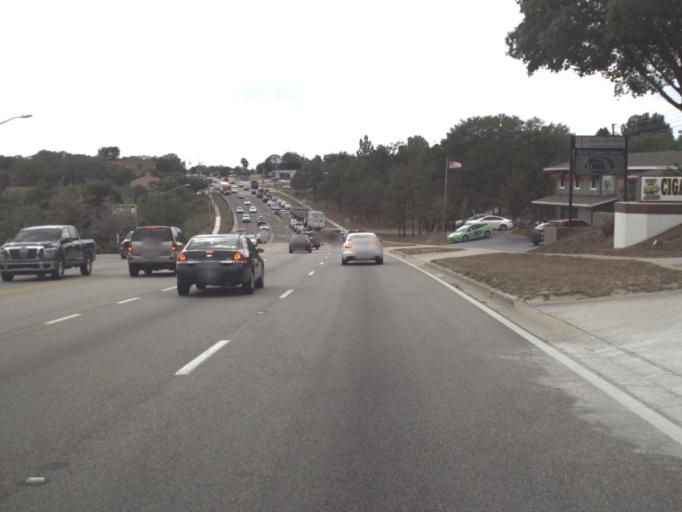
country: US
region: Florida
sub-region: Lake County
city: Clermont
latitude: 28.5507
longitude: -81.7521
